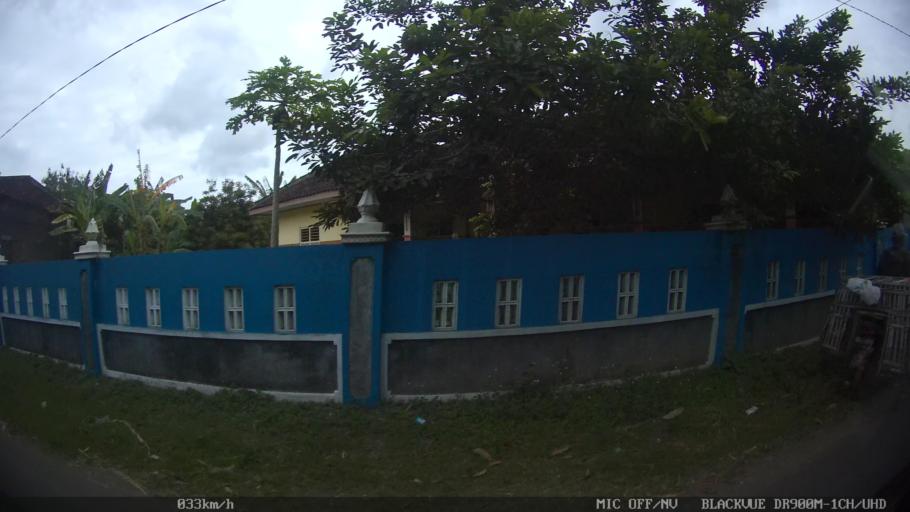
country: ID
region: Daerah Istimewa Yogyakarta
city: Sewon
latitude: -7.8774
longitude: 110.4172
